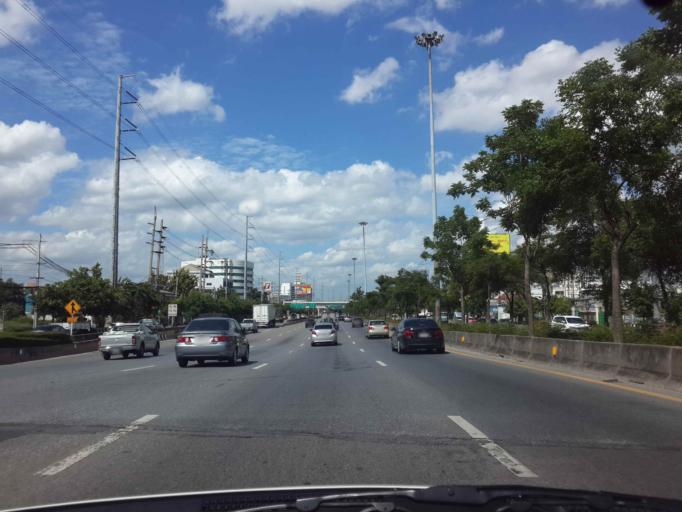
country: TH
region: Bangkok
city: Bang Khun Thian
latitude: 13.6539
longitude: 100.4260
